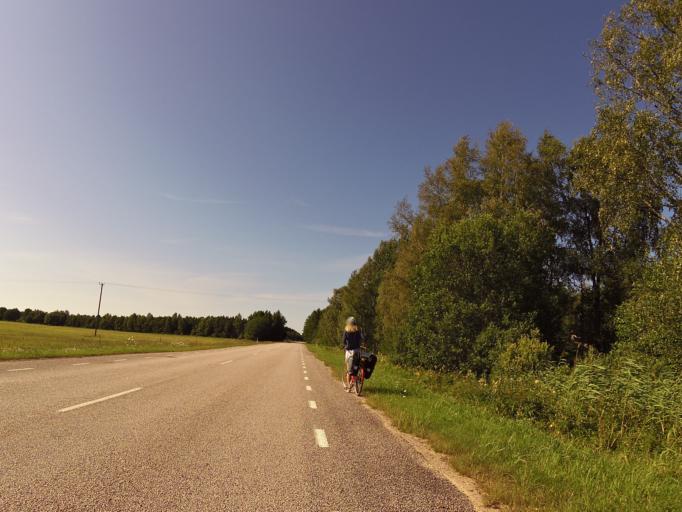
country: EE
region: Hiiumaa
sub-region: Kaerdla linn
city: Kardla
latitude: 58.7413
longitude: 22.5309
